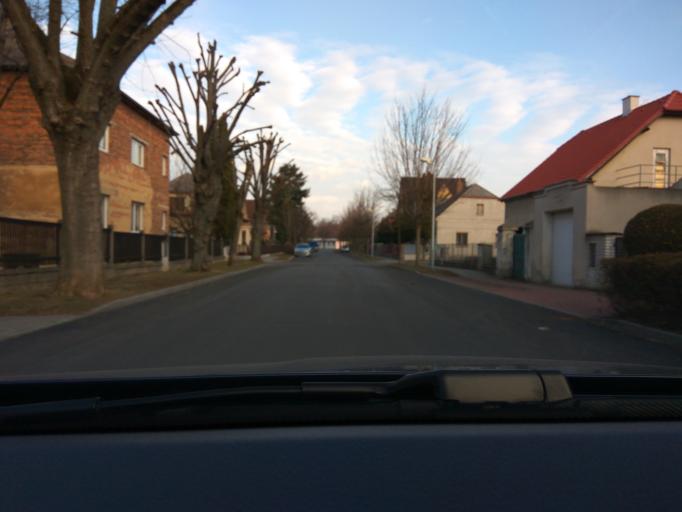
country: CZ
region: Praha
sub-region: Praha 18
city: Letnany
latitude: 50.1531
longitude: 14.5258
